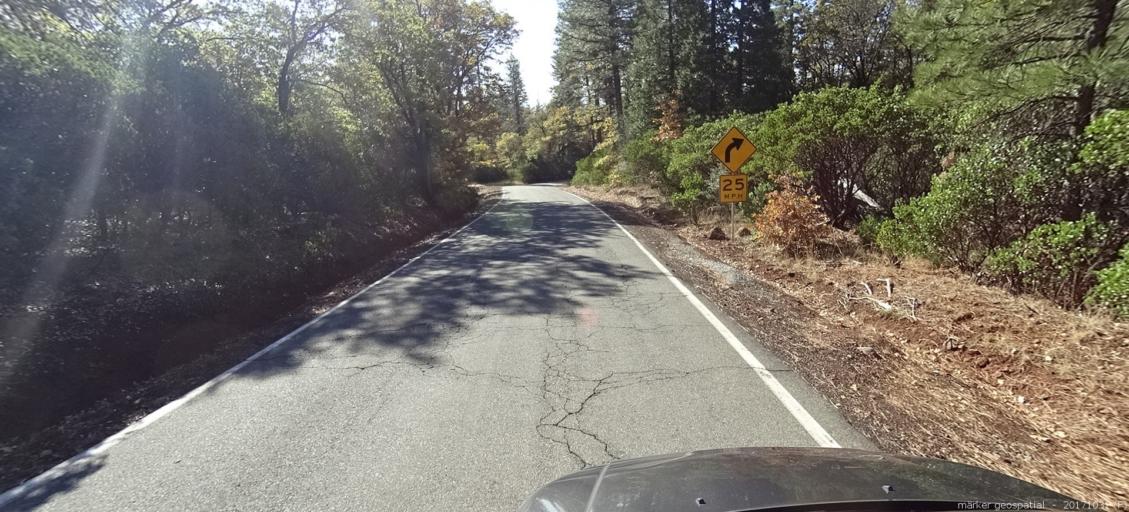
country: US
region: California
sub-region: Shasta County
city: Shingletown
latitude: 40.4746
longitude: -121.8754
